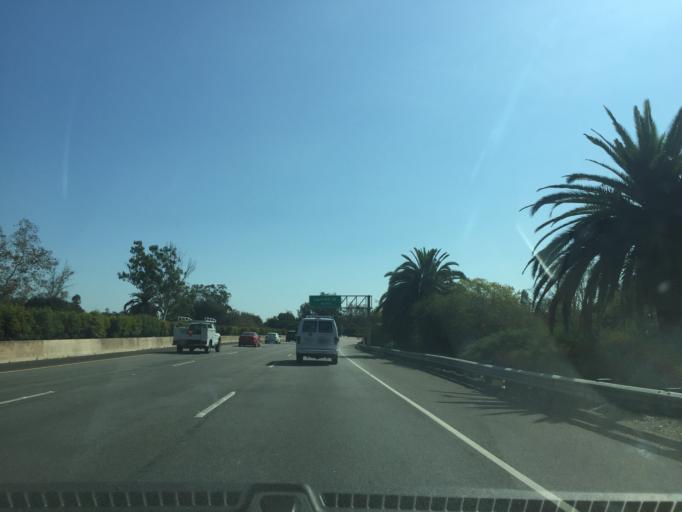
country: US
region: California
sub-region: Santa Barbara County
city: Santa Barbara
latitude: 34.4260
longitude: -119.7226
